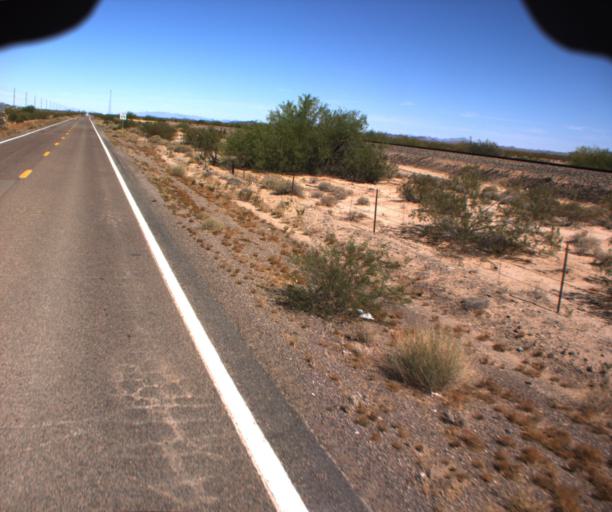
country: US
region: Arizona
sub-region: La Paz County
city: Salome
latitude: 33.8265
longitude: -113.8702
